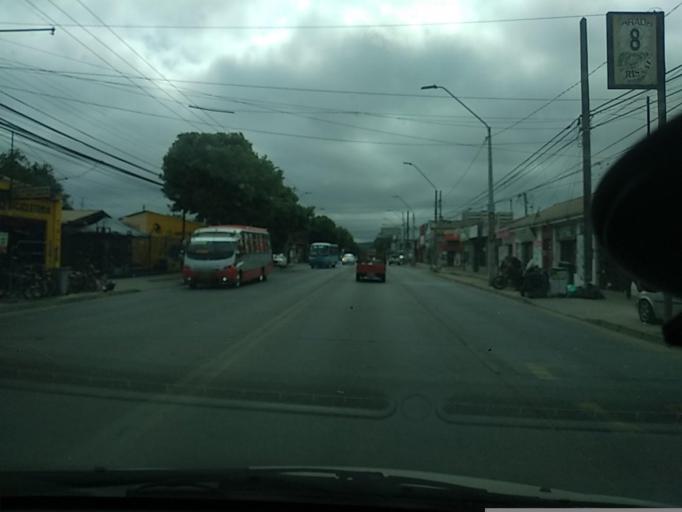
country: CL
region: Valparaiso
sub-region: Provincia de Marga Marga
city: Villa Alemana
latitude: -33.0444
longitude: -71.3828
